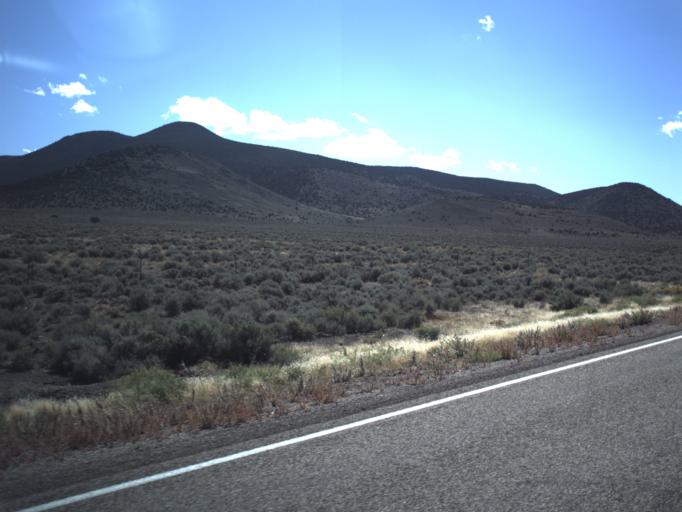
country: US
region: Utah
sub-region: Beaver County
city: Milford
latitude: 38.1676
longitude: -112.9540
